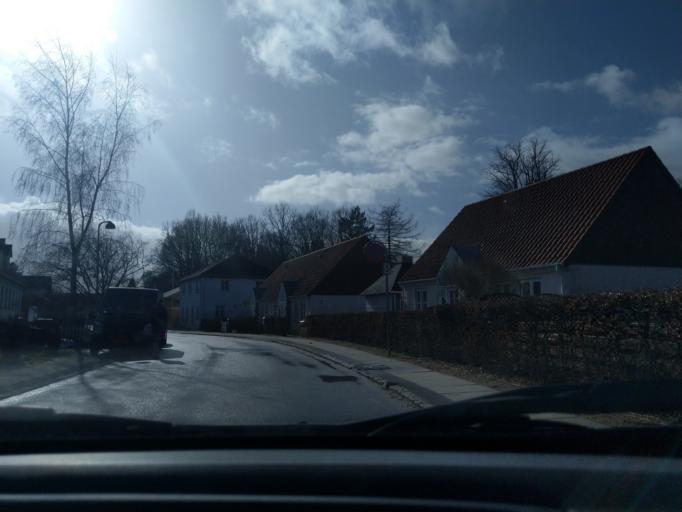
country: DK
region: Zealand
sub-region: Naestved Kommune
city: Naestved
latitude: 55.3157
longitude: 11.6781
